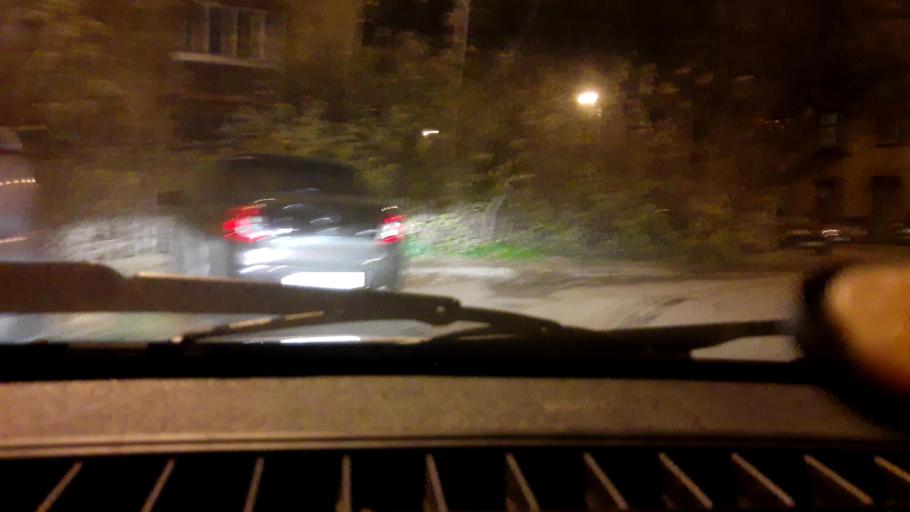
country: RU
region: Bashkortostan
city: Ufa
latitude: 54.7949
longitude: 56.1433
